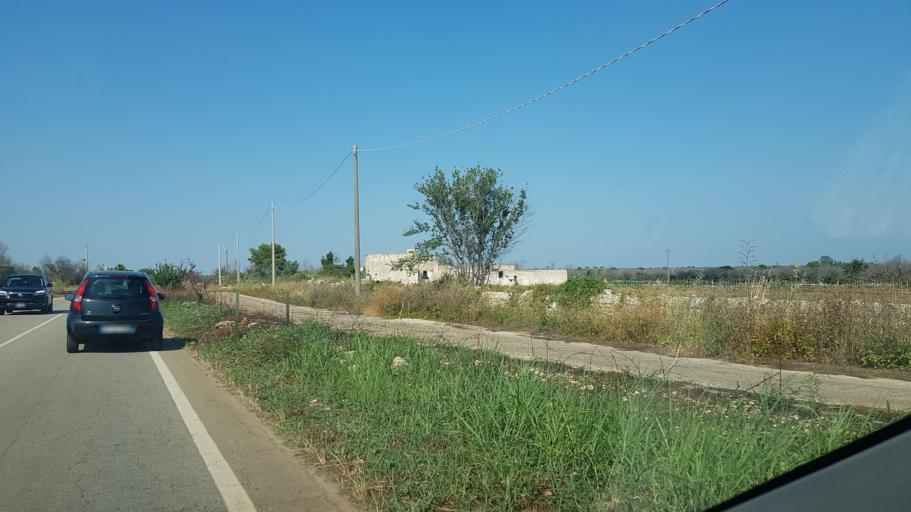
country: IT
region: Apulia
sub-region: Provincia di Lecce
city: Acquarica del Capo
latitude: 39.8786
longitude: 18.2291
